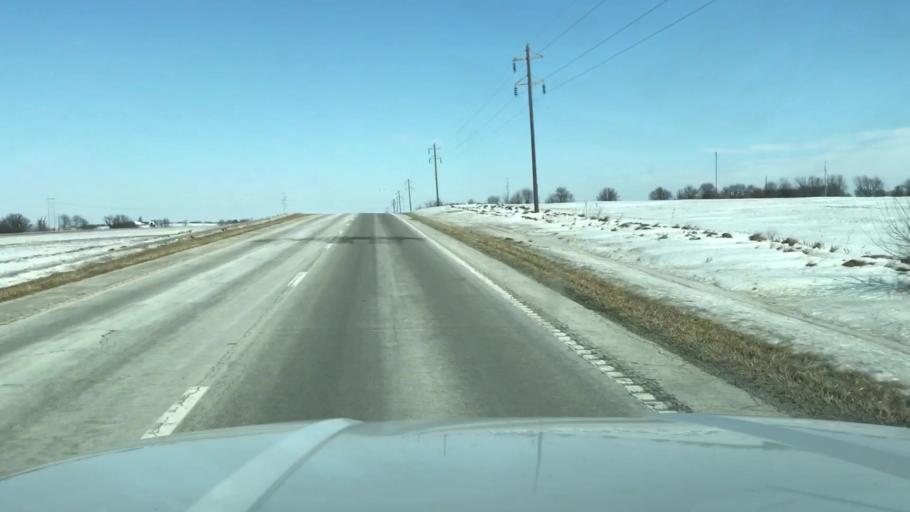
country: US
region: Missouri
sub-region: Nodaway County
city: Maryville
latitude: 40.1582
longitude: -94.8690
